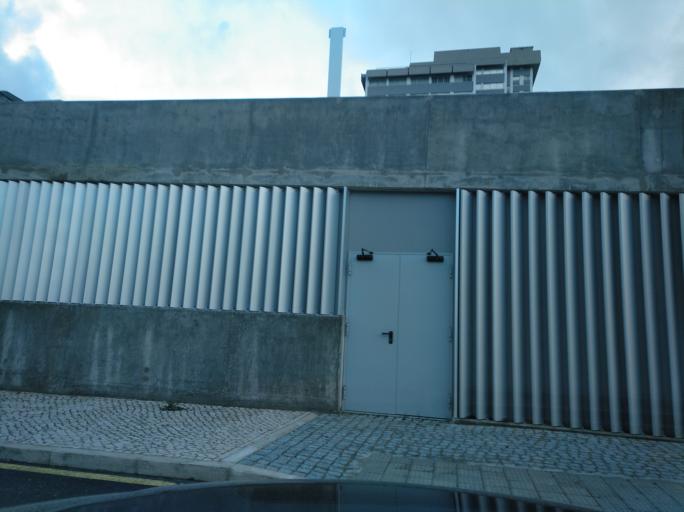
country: PT
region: Lisbon
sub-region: Lisbon
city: Lisbon
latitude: 38.7451
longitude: -9.1299
